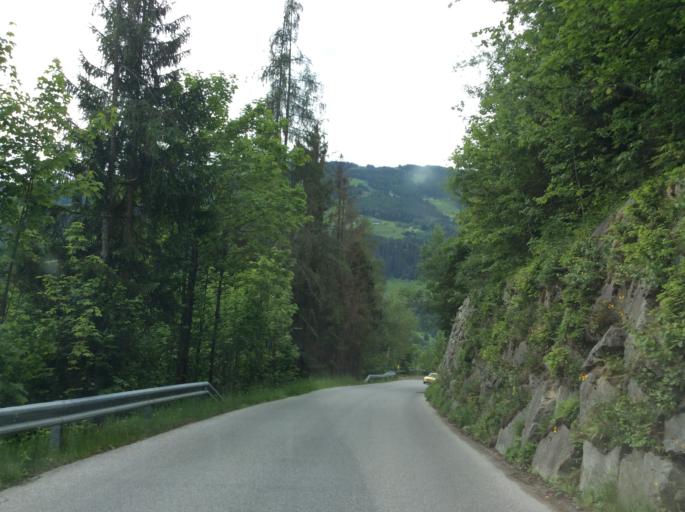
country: AT
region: Styria
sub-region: Politischer Bezirk Liezen
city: Schladming
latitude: 47.4047
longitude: 13.6943
